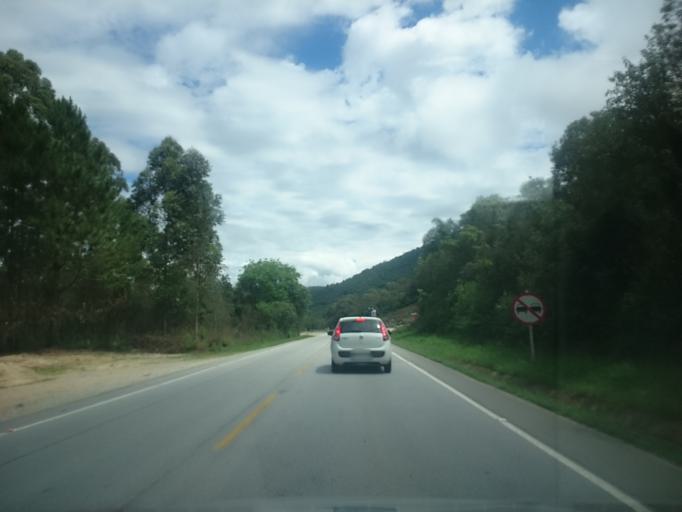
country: BR
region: Santa Catarina
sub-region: Anitapolis
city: Anitapolis
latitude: -27.6915
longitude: -49.2304
